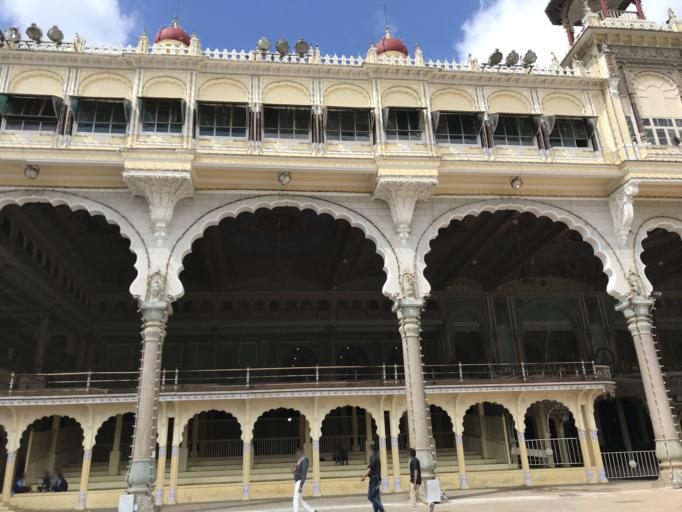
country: IN
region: Karnataka
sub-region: Mysore
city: Mysore
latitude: 12.3050
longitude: 76.6551
